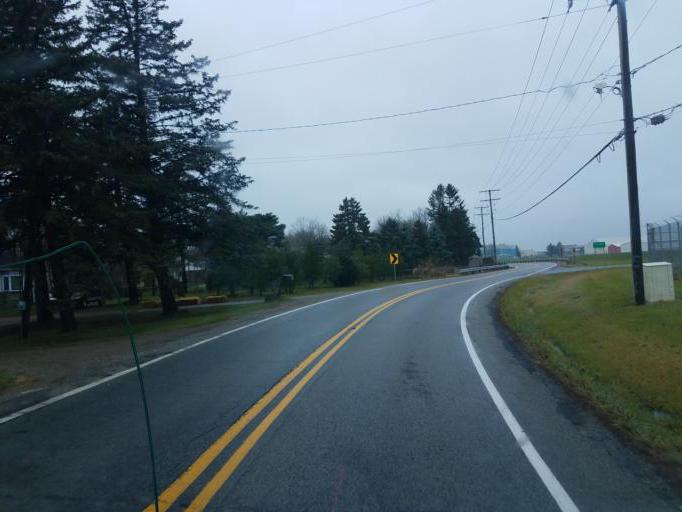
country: US
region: Ohio
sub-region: Franklin County
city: Dublin
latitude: 40.0724
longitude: -83.0682
